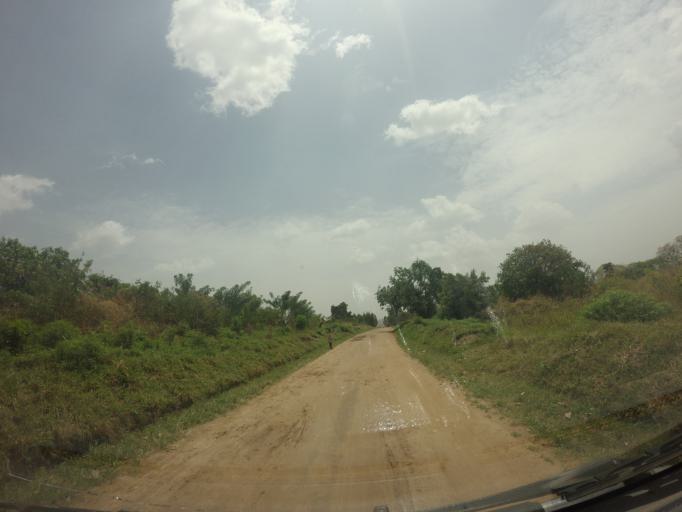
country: UG
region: Northern Region
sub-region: Arua District
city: Arua
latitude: 2.9390
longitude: 30.9154
